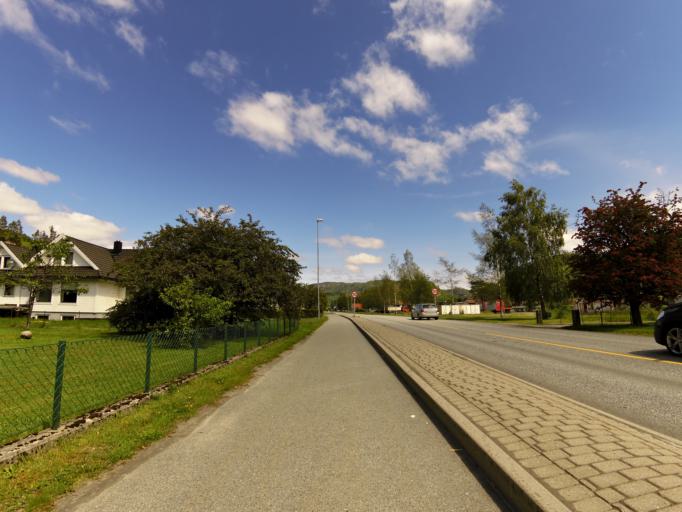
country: NO
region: Vest-Agder
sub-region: Kvinesdal
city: Liknes
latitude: 58.3074
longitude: 6.9563
